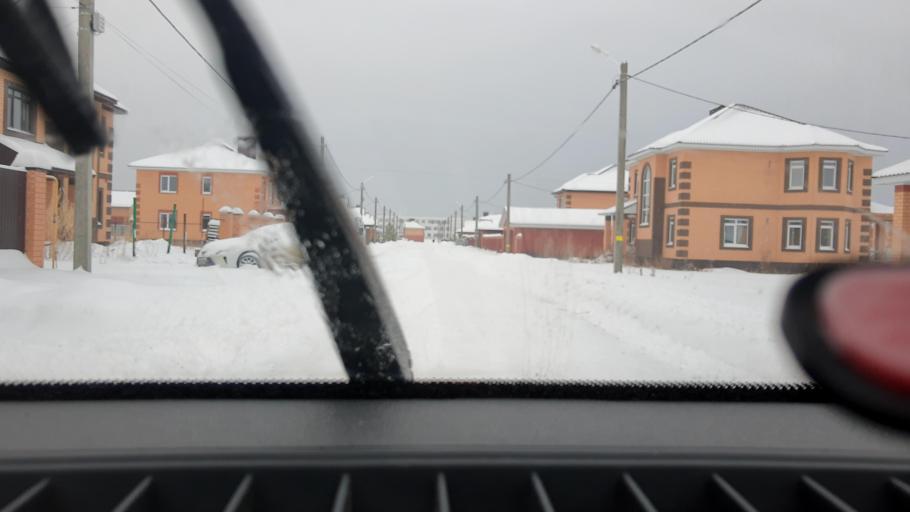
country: RU
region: Bashkortostan
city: Ufa
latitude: 54.6172
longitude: 55.8826
